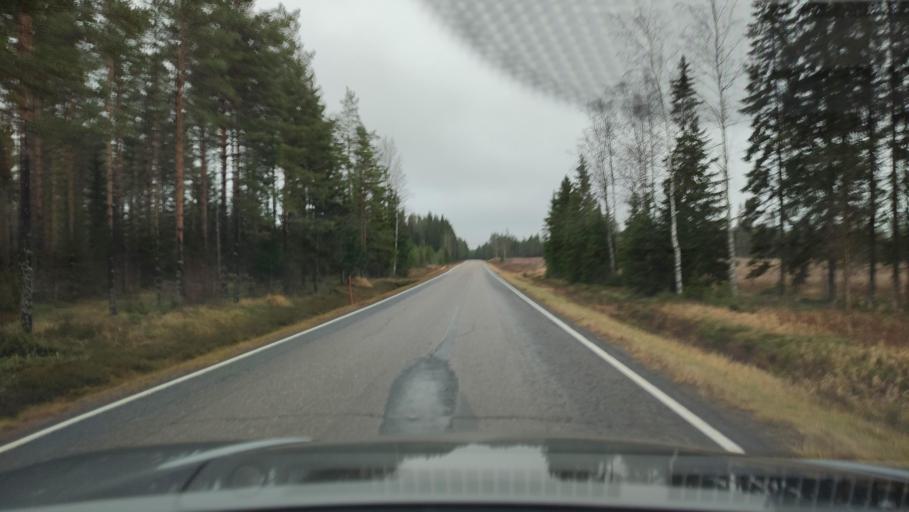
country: FI
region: Southern Ostrobothnia
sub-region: Suupohja
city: Isojoki
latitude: 62.2147
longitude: 21.9868
